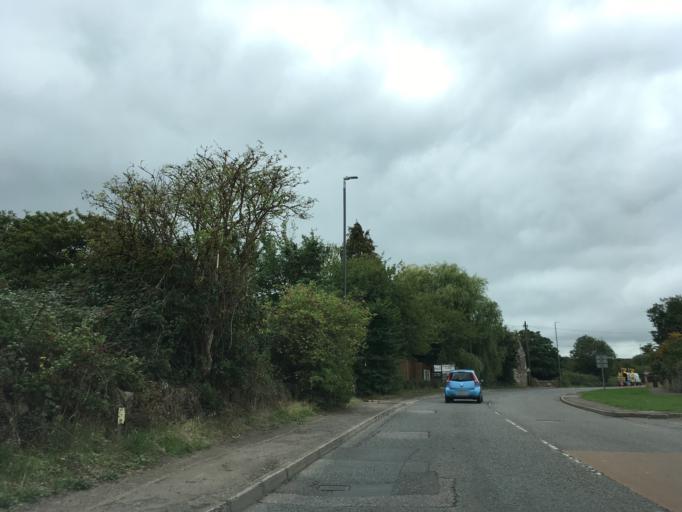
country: GB
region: England
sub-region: South Gloucestershire
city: Bitton
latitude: 51.4386
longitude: -2.4713
